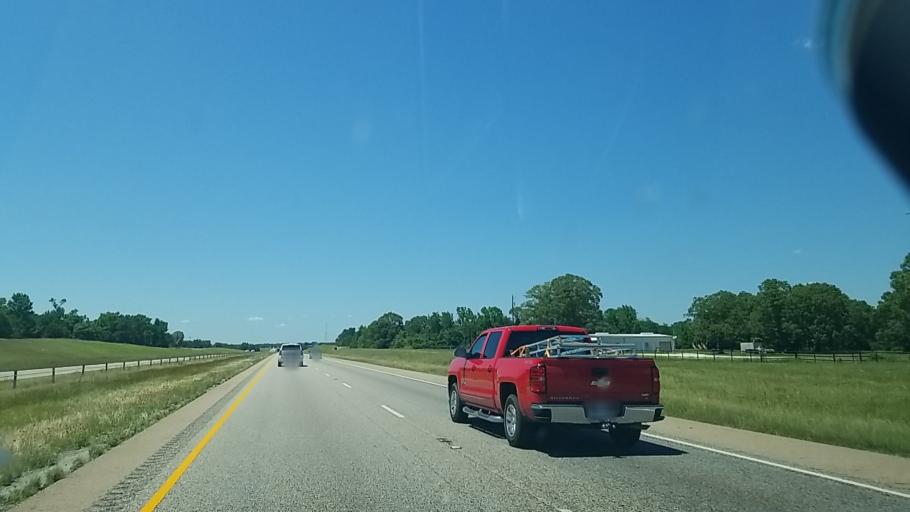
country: US
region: Texas
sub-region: Leon County
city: Buffalo
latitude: 31.3998
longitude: -96.0347
